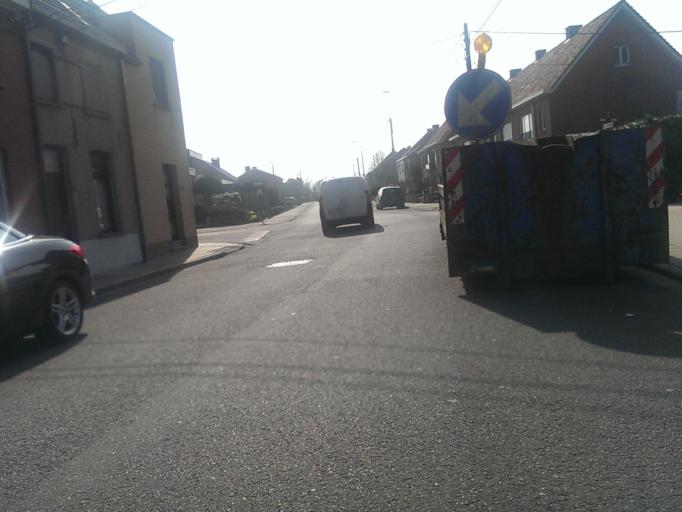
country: BE
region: Flanders
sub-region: Provincie West-Vlaanderen
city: Roeselare
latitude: 50.9323
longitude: 3.1231
